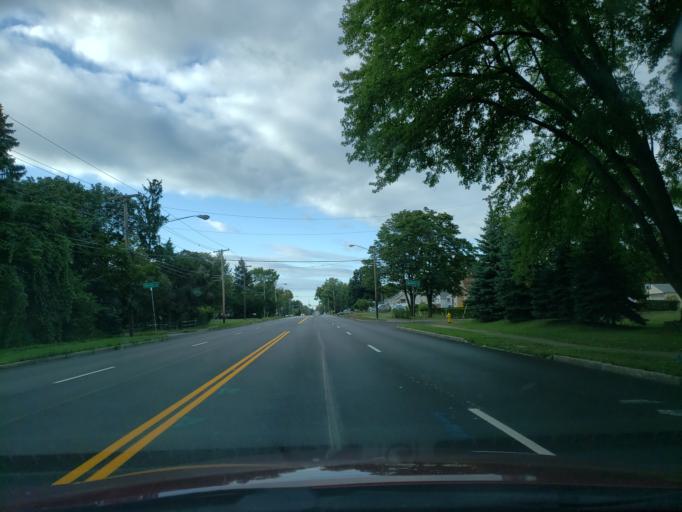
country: US
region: New York
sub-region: Monroe County
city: Greece
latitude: 43.2355
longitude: -77.6591
